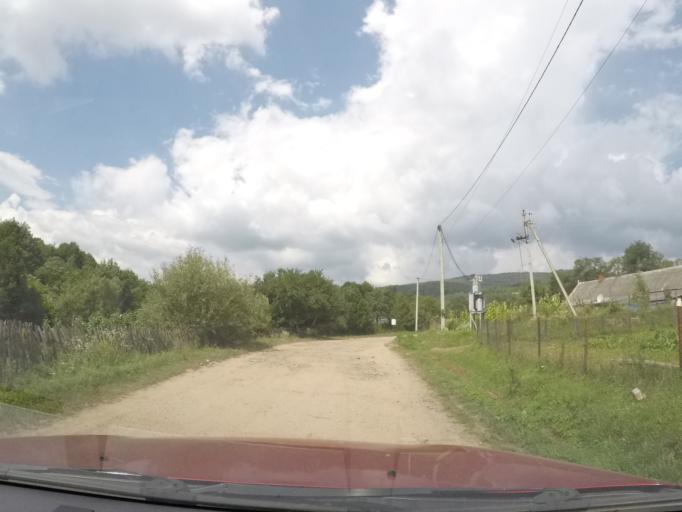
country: UA
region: Zakarpattia
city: Velykyi Bereznyi
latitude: 49.0325
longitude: 22.5817
